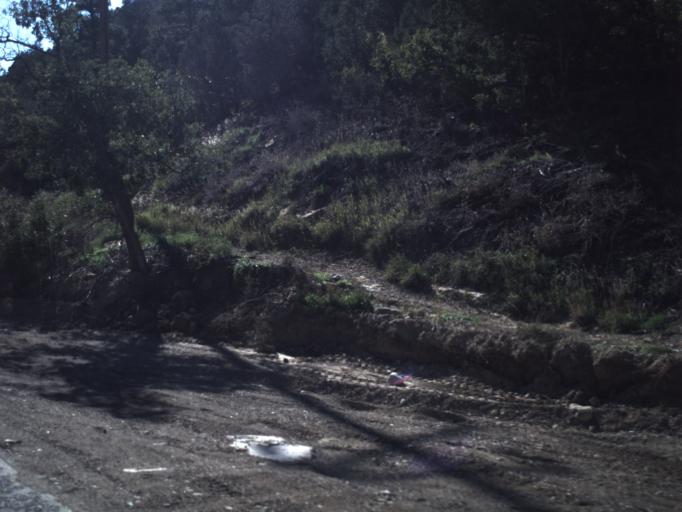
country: US
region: Utah
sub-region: Iron County
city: Parowan
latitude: 37.7878
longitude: -112.8254
